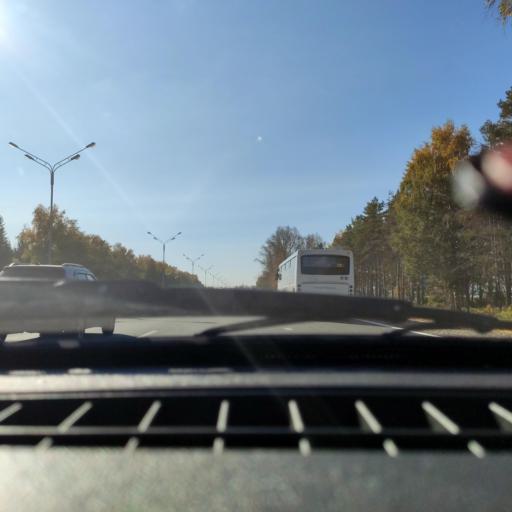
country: RU
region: Bashkortostan
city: Ufa
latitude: 54.5931
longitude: 55.9129
